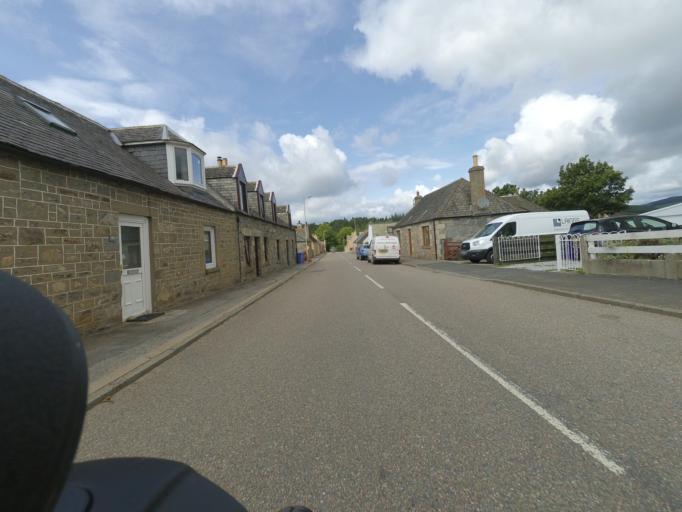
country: GB
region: Scotland
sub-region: Highland
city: Grantown on Spey
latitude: 57.2552
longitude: -3.3840
